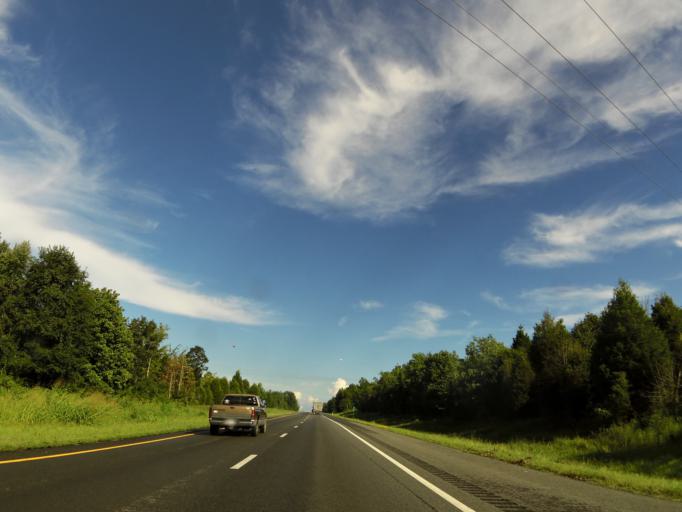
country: US
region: Kentucky
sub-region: Todd County
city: Guthrie
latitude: 36.5128
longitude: -87.2057
